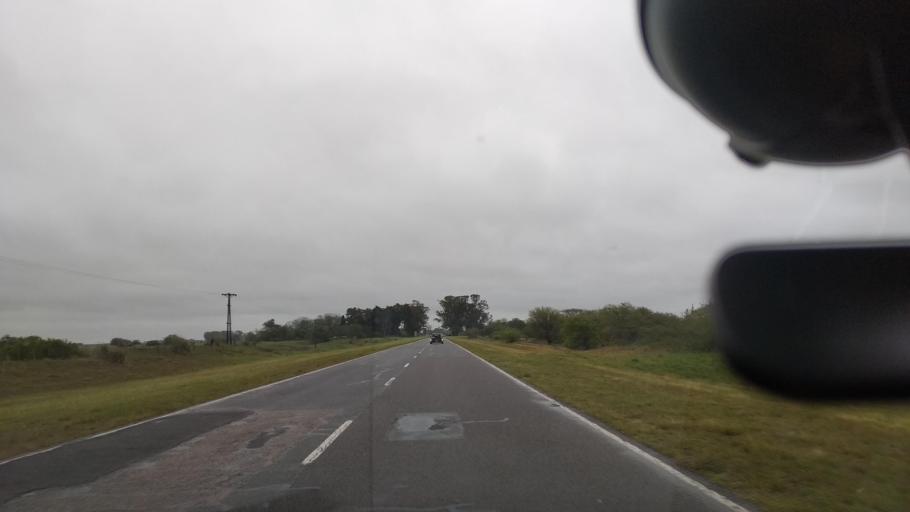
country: AR
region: Buenos Aires
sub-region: Partido de Castelli
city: Castelli
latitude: -36.0160
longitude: -57.4473
